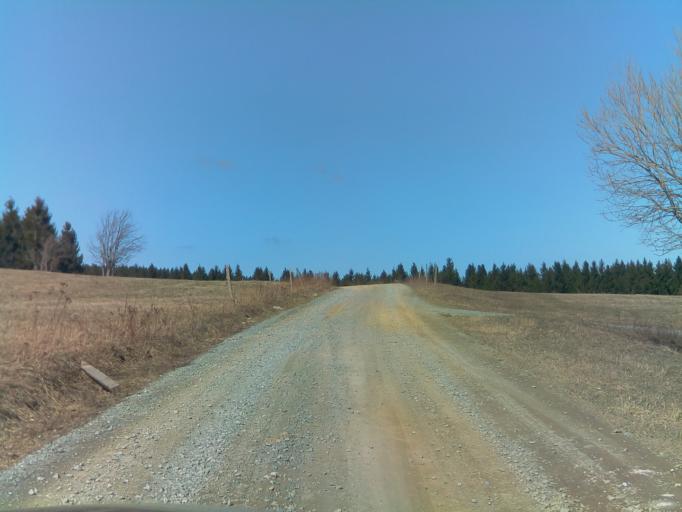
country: DE
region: Thuringia
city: Steinheid
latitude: 50.4567
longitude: 11.0994
